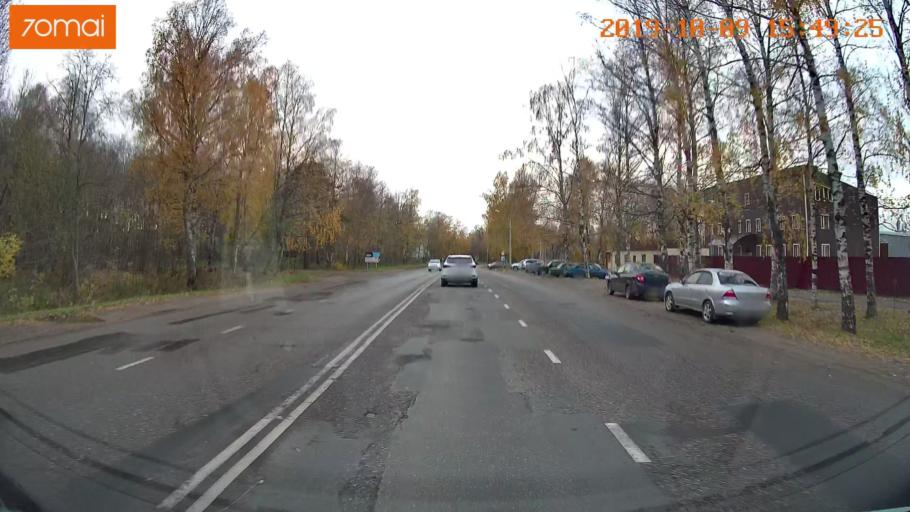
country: RU
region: Kostroma
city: Oktyabr'skiy
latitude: 57.8052
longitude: 41.0050
